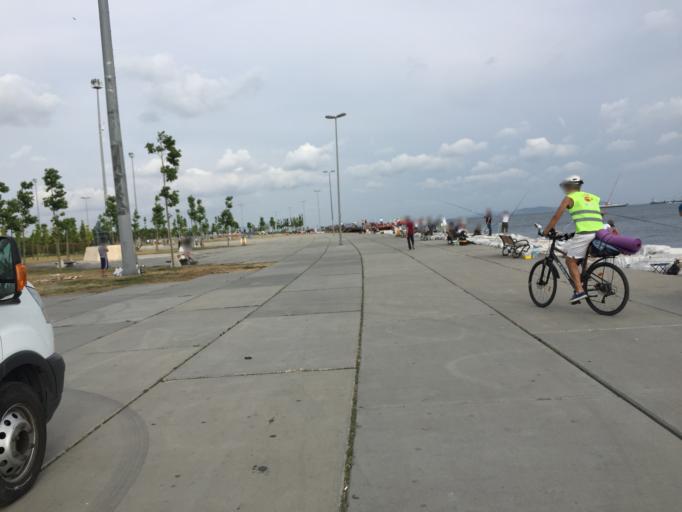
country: TR
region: Istanbul
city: Istanbul
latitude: 40.9975
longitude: 28.9409
